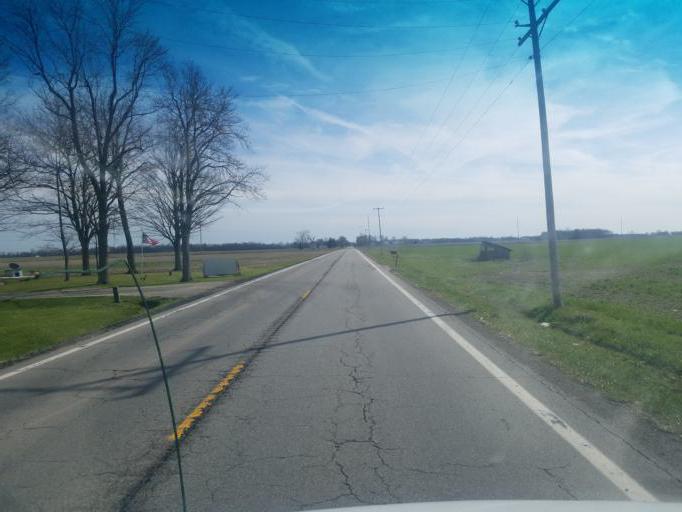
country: US
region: Ohio
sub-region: Union County
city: Richwood
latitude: 40.4085
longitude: -83.2580
